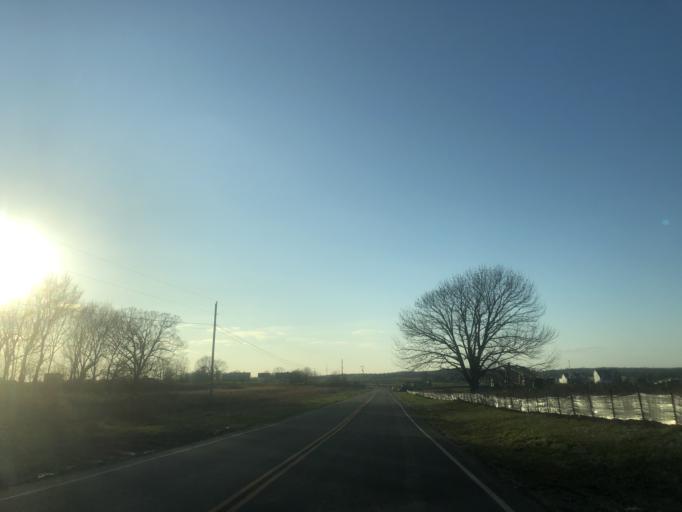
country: US
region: Tennessee
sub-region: Sumner County
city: White House
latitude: 36.4813
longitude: -86.7021
